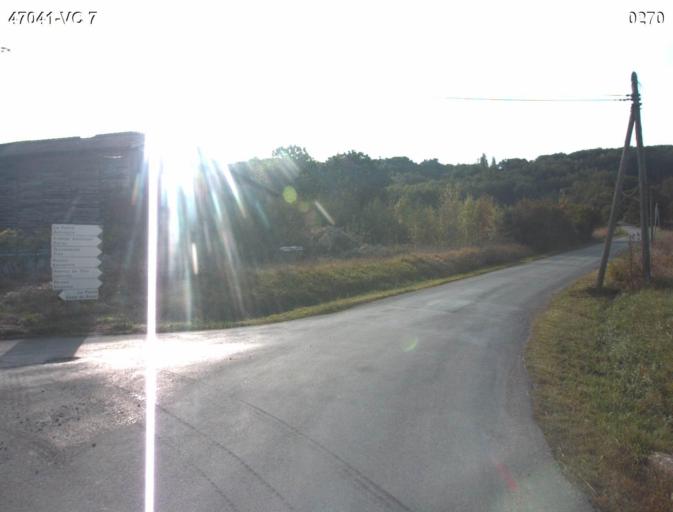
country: FR
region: Aquitaine
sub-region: Departement du Lot-et-Garonne
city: Port-Sainte-Marie
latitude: 44.2033
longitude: 0.4135
